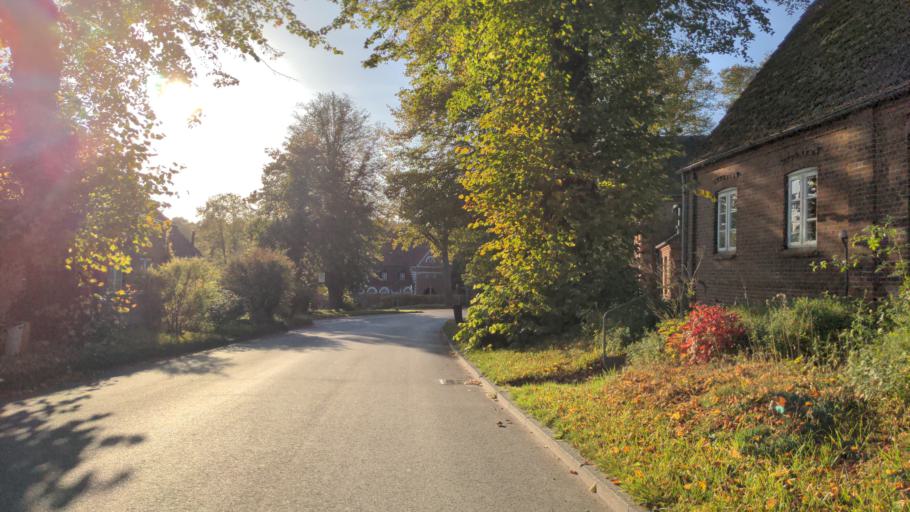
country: DE
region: Schleswig-Holstein
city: Pronstorf
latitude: 53.9573
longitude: 10.4700
